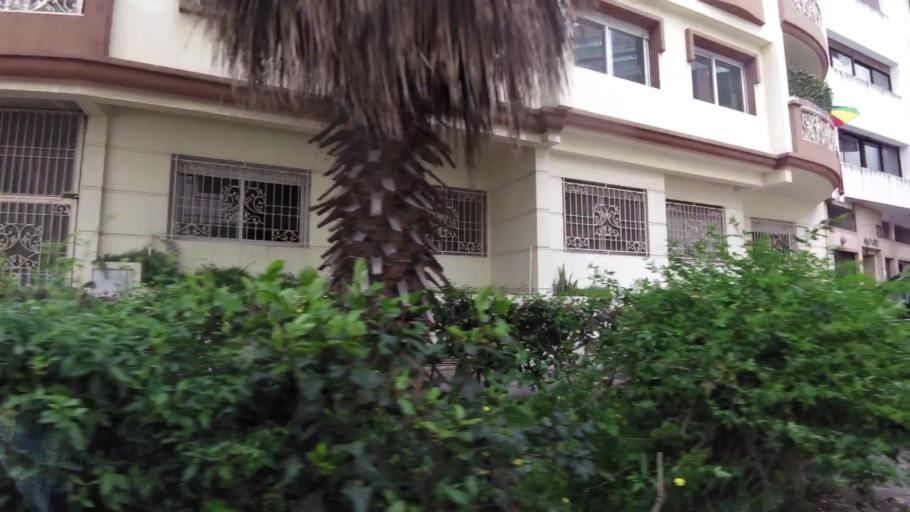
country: MA
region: Grand Casablanca
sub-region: Casablanca
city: Casablanca
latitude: 33.5747
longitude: -7.6492
